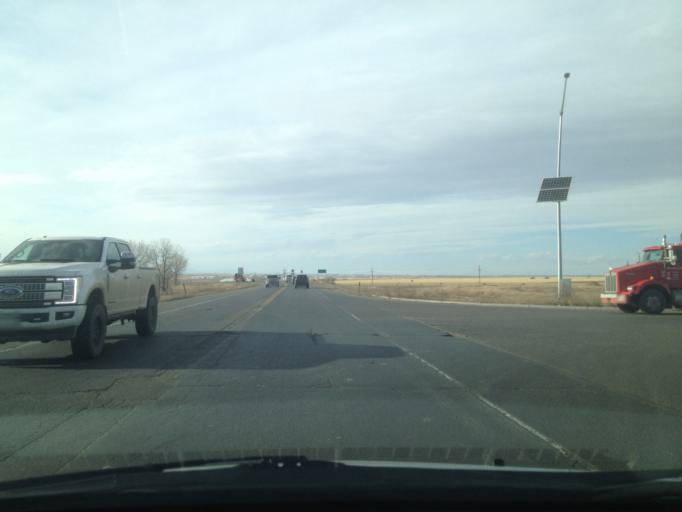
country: US
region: Colorado
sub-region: Weld County
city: Hudson
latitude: 40.0779
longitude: -104.6509
